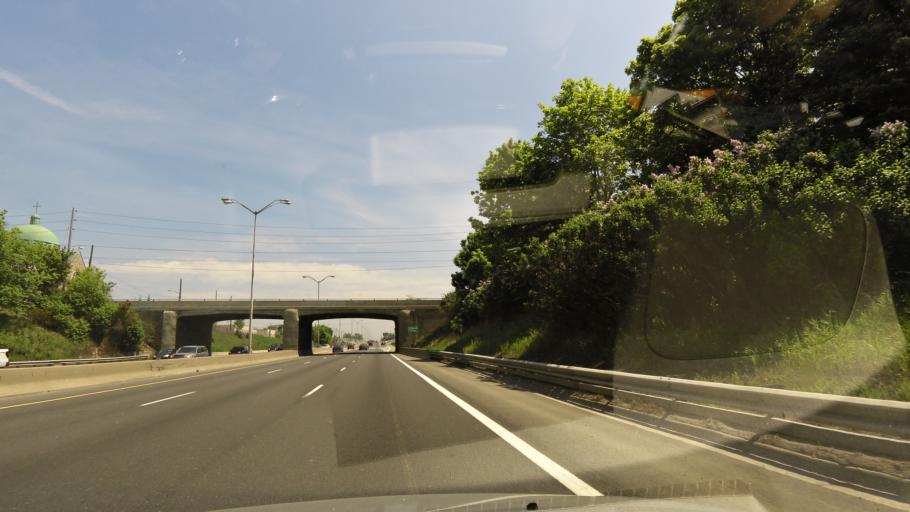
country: CA
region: Ontario
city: Oshawa
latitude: 43.8816
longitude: -78.8553
